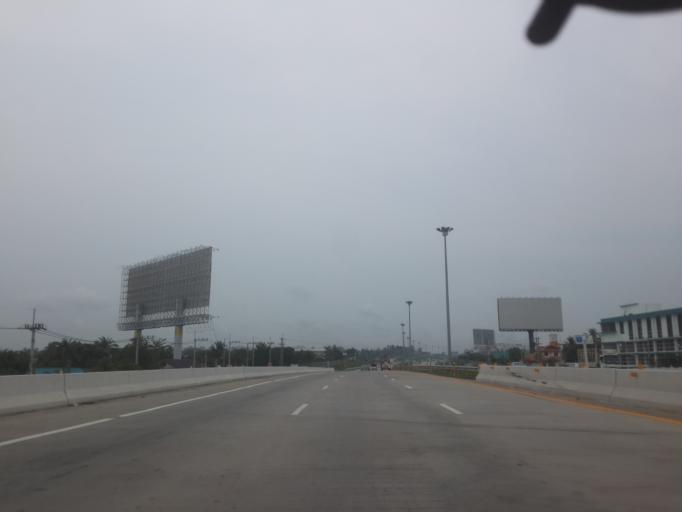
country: TH
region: Chon Buri
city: Phatthaya
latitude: 12.9509
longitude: 100.9407
